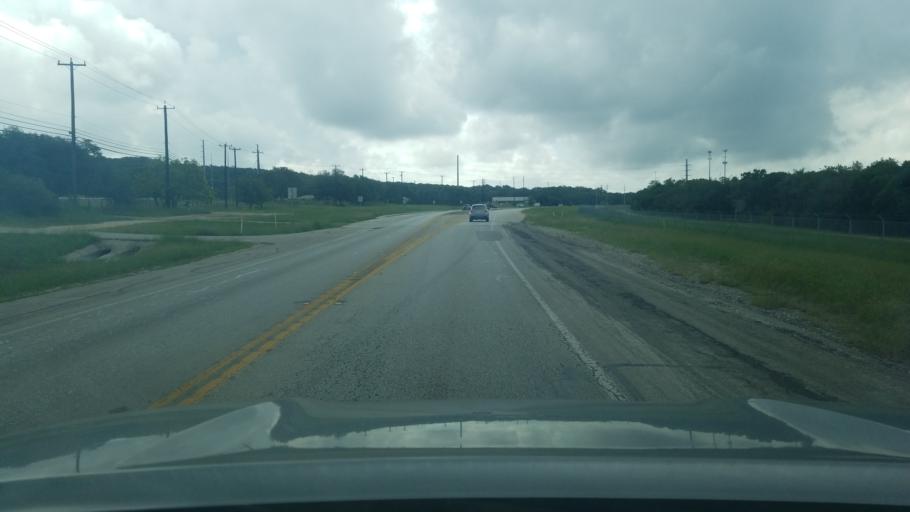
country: US
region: Texas
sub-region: Bexar County
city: Timberwood Park
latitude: 29.6686
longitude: -98.5212
